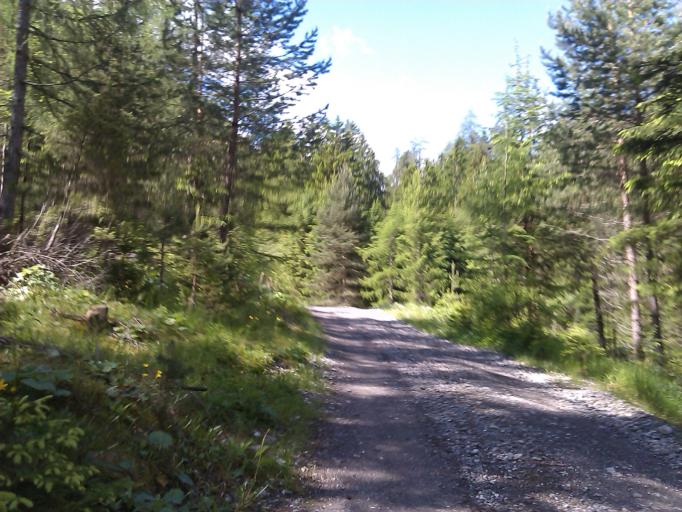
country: AT
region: Tyrol
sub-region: Politischer Bezirk Reutte
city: Biberwier
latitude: 47.3607
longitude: 10.8671
